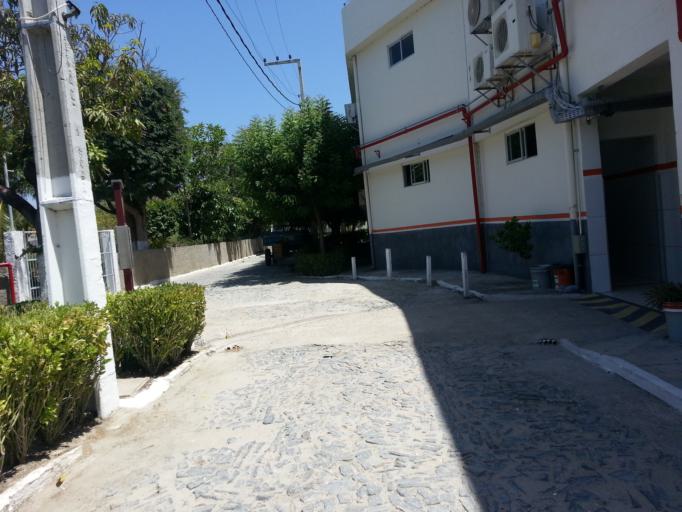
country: BR
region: Ceara
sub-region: Quixada
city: Quixada
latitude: -4.9744
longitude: -39.0141
